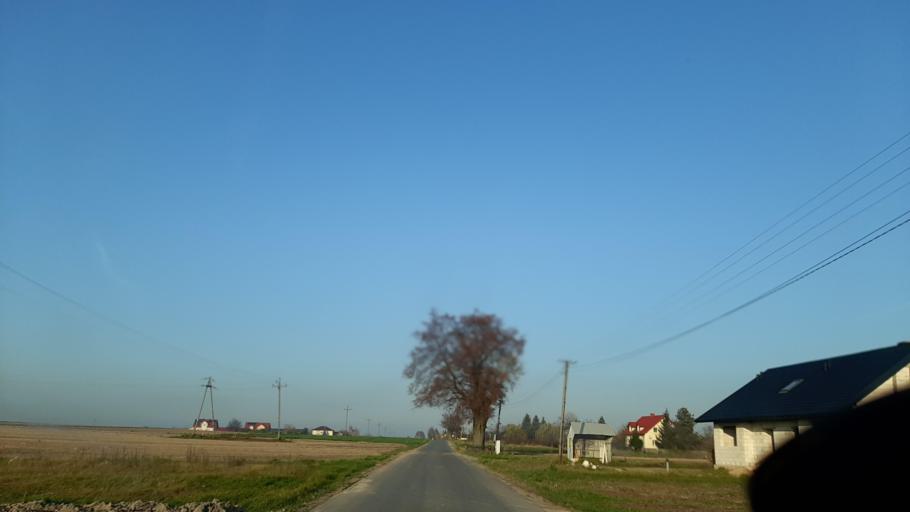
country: PL
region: Lublin Voivodeship
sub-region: Powiat lubelski
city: Garbow
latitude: 51.3776
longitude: 22.3326
